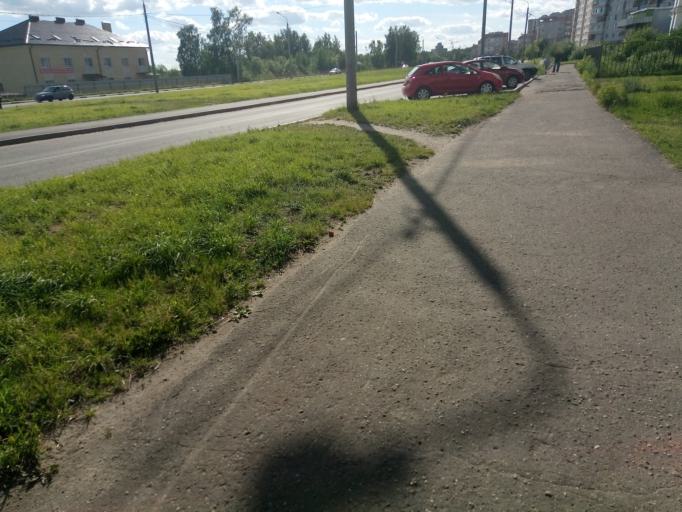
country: RU
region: Jaroslavl
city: Yaroslavl
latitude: 57.6375
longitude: 39.9587
